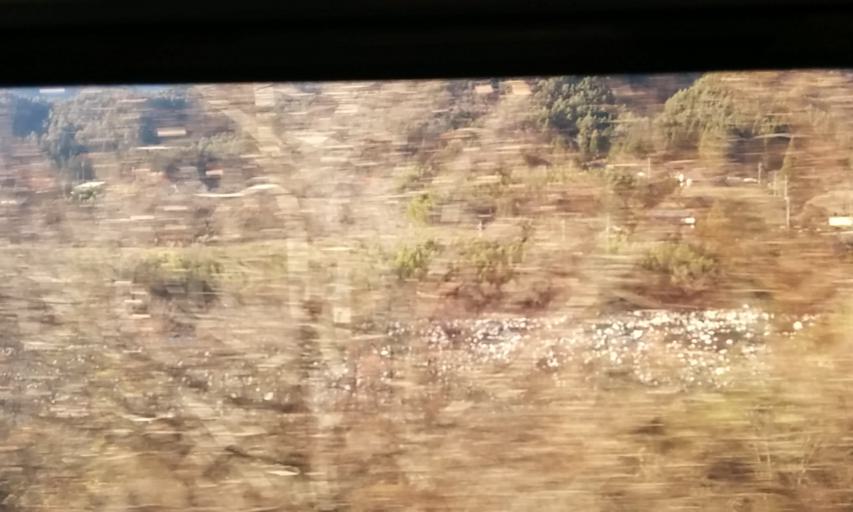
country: JP
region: Nagano
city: Iida
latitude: 35.7022
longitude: 137.6983
